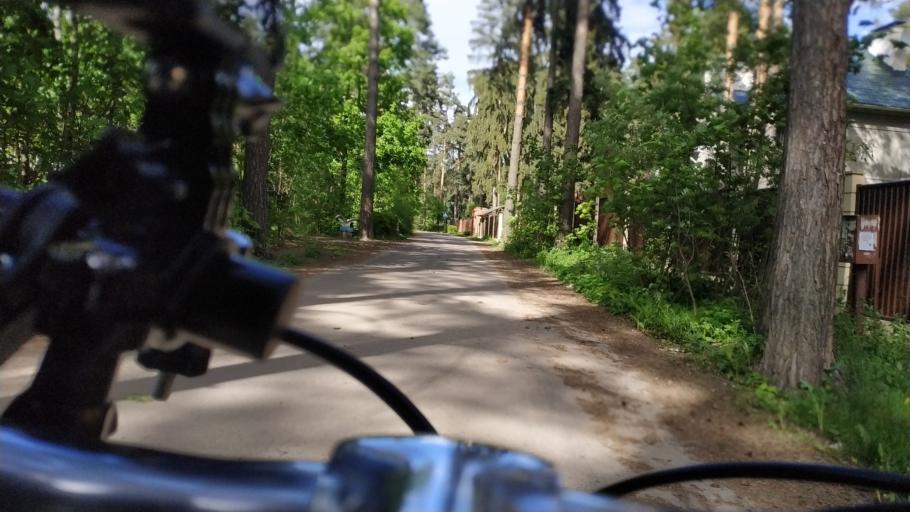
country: RU
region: Moskovskaya
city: Kratovo
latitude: 55.5729
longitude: 38.1934
